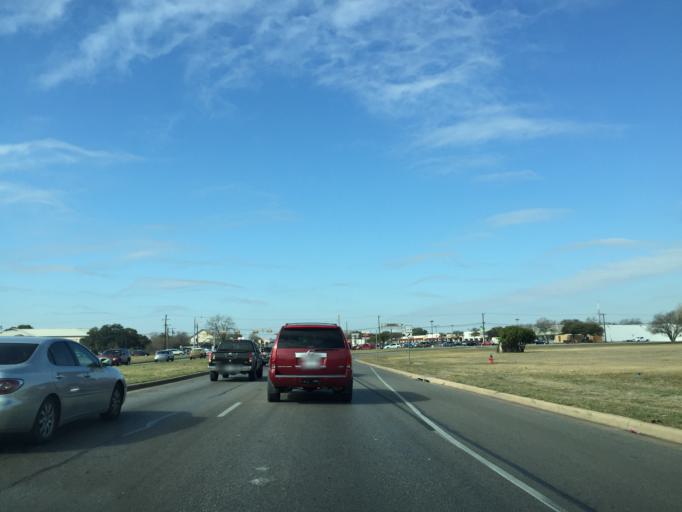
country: US
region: Texas
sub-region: Williamson County
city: Round Rock
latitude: 30.5184
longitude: -97.6812
